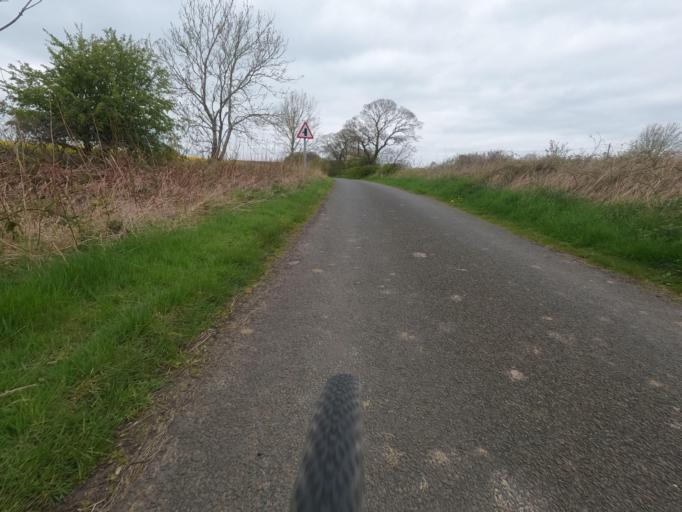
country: GB
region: England
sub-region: Northumberland
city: Horsley
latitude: 55.0594
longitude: -1.8451
